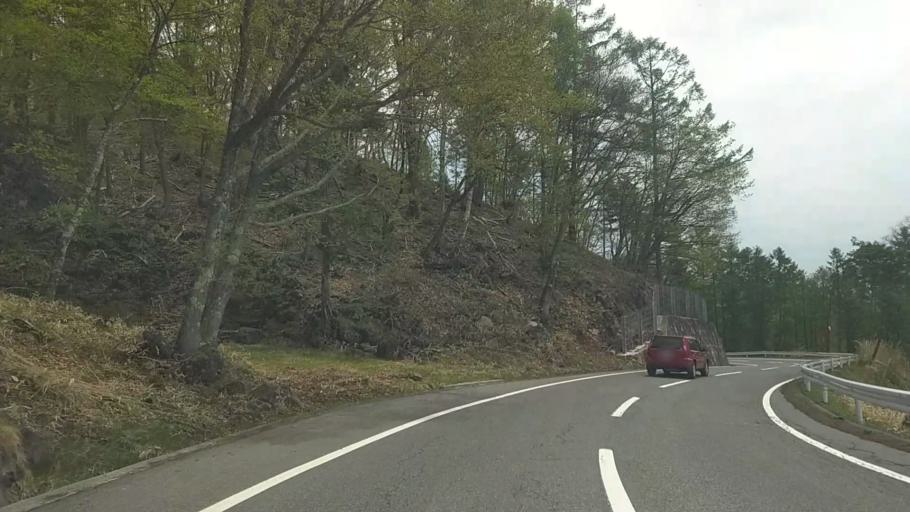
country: JP
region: Nagano
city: Chino
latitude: 36.0407
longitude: 138.2813
